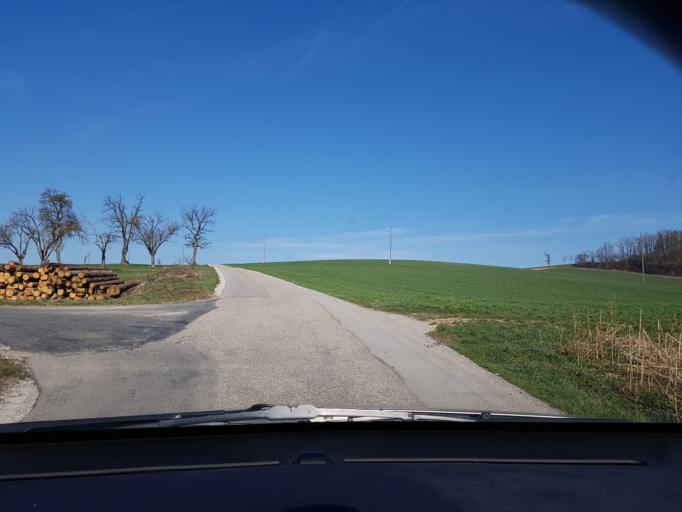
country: AT
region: Upper Austria
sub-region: Politischer Bezirk Linz-Land
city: Ansfelden
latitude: 48.1928
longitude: 14.3232
